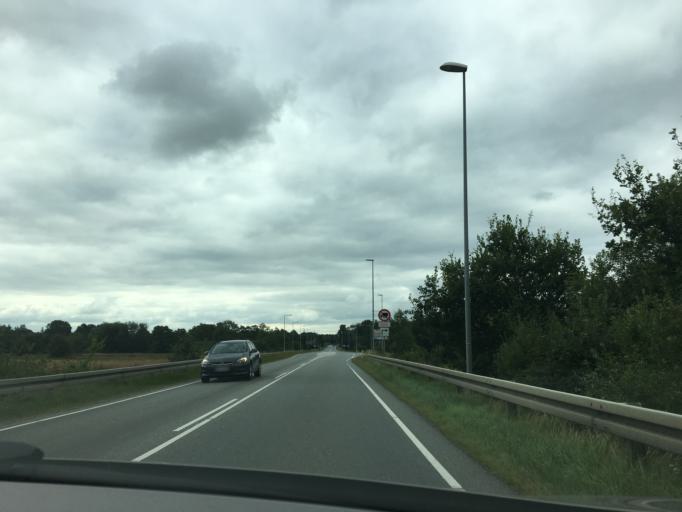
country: DK
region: Central Jutland
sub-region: Herning Kommune
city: Kibaek
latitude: 55.9436
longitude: 8.7908
